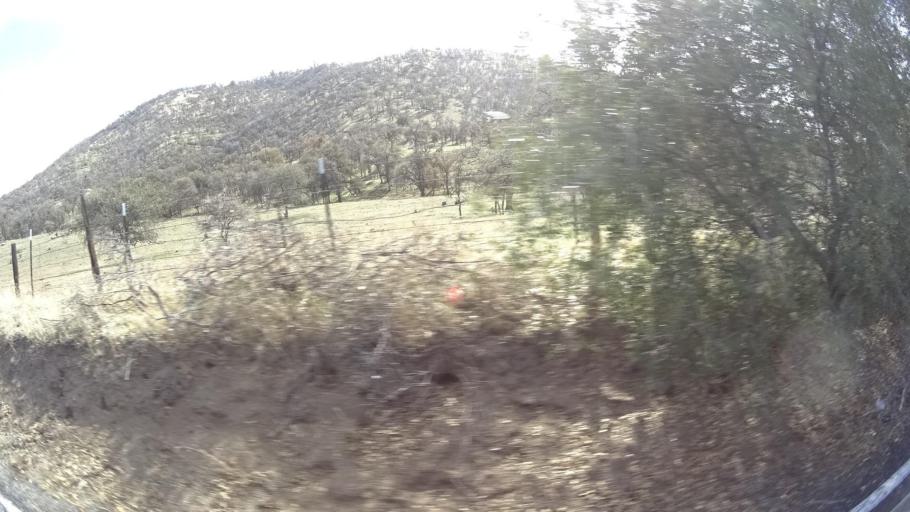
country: US
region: California
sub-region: Kern County
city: Alta Sierra
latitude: 35.6440
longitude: -118.7986
